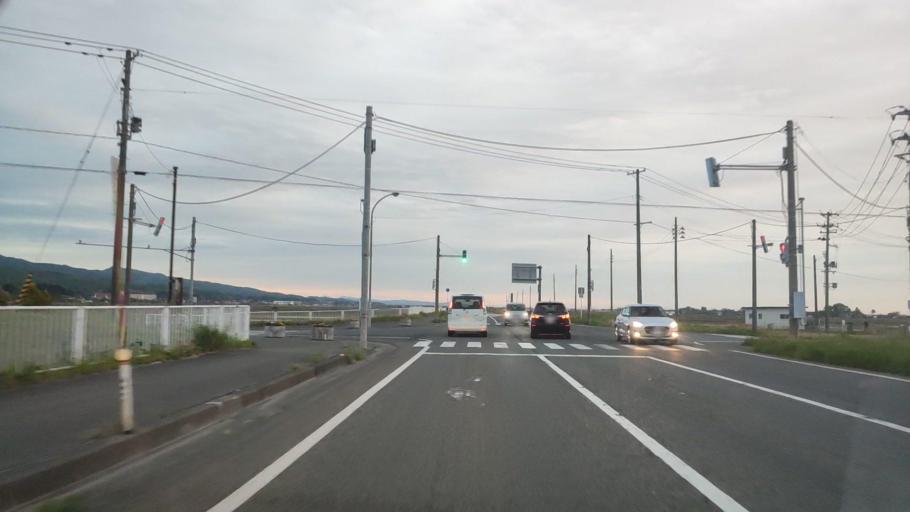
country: JP
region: Niigata
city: Niitsu-honcho
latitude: 37.7715
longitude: 139.1031
